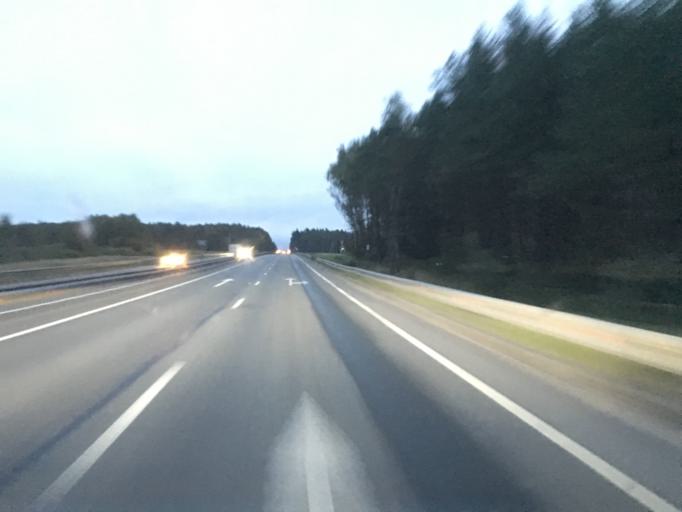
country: RU
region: Kaluga
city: Maloyaroslavets
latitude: 54.9659
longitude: 36.4716
